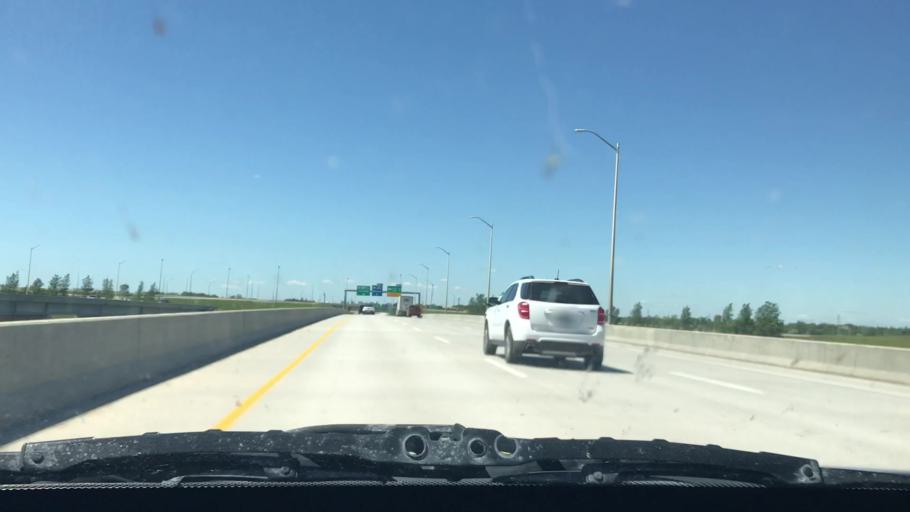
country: CA
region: Manitoba
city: Winnipeg
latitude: 49.8312
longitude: -96.9546
